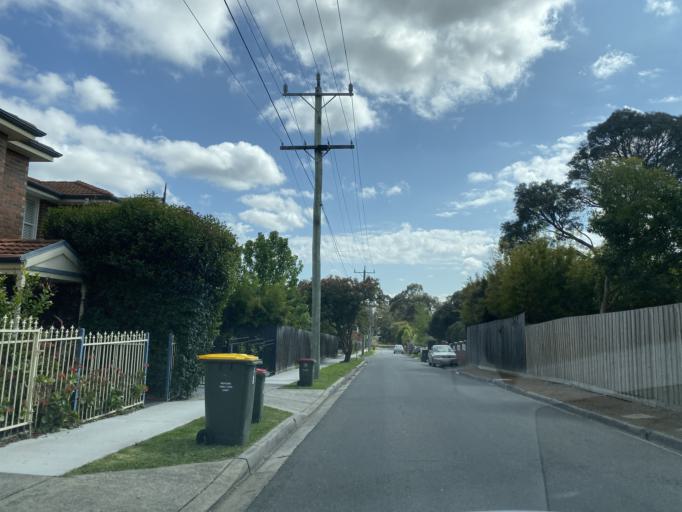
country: AU
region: Victoria
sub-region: Whitehorse
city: Burwood
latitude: -37.8464
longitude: 145.1244
